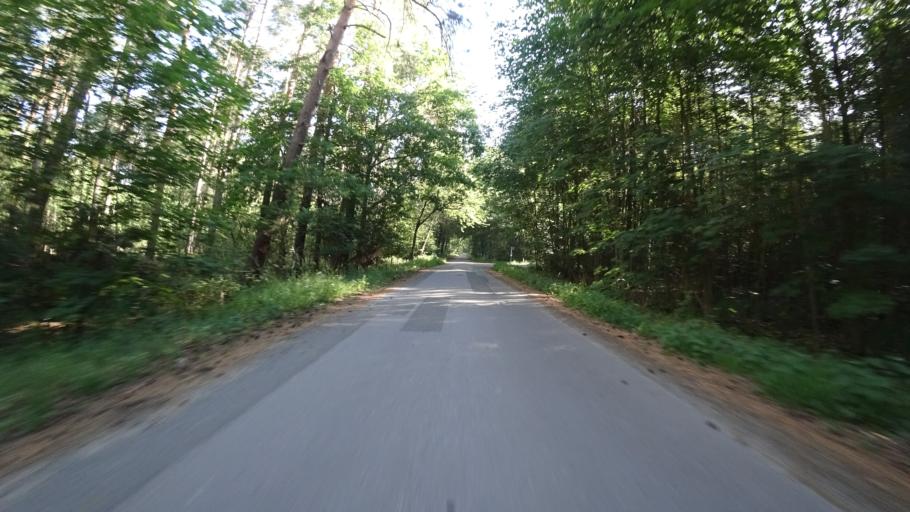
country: DE
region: North Rhine-Westphalia
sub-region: Regierungsbezirk Detmold
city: Rheda-Wiedenbruck
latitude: 51.8826
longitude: 8.3173
